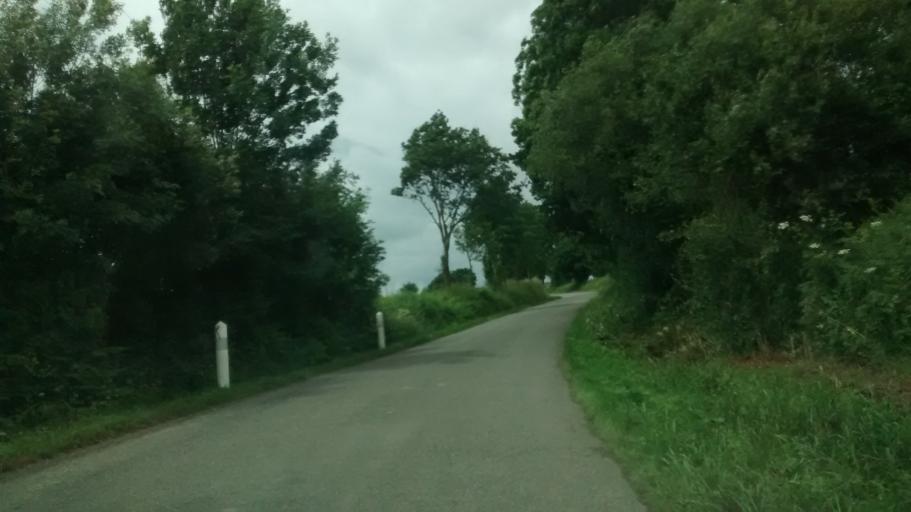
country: FR
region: Brittany
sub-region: Departement du Morbihan
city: Carentoir
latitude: 47.8015
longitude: -2.1122
